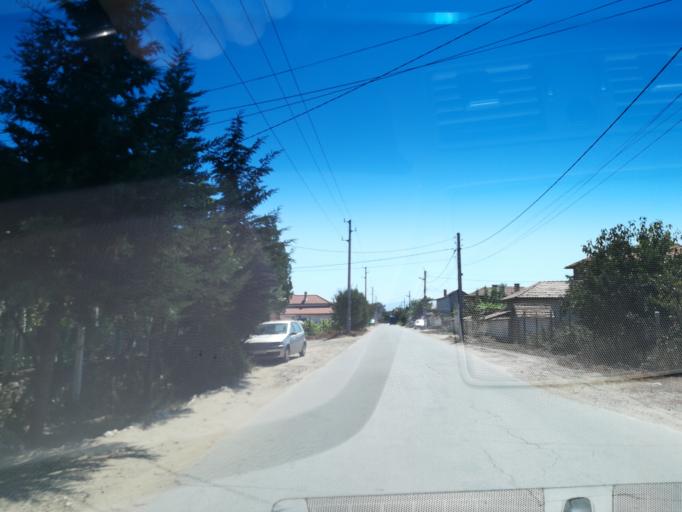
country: BG
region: Pazardzhik
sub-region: Obshtina Pazardzhik
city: Pazardzhik
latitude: 42.2819
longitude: 24.3948
